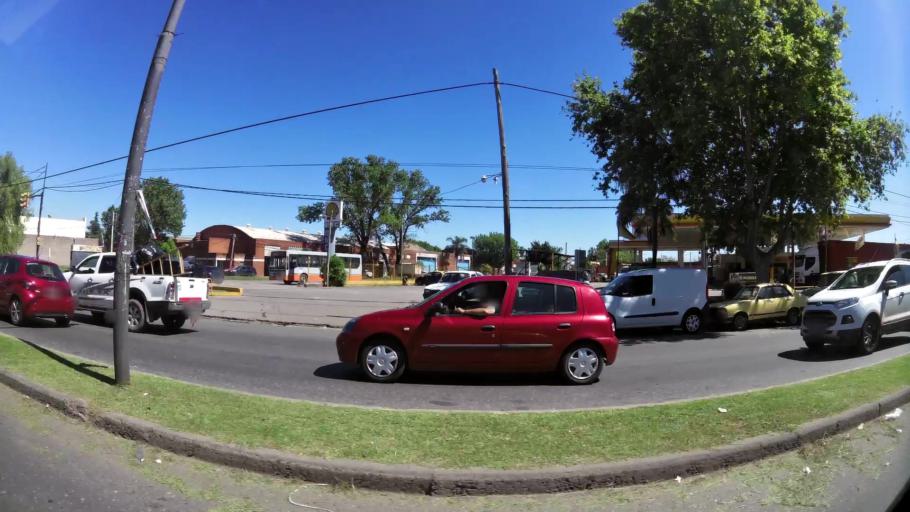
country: AR
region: Santa Fe
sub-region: Departamento de Rosario
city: Rosario
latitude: -32.9627
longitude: -60.7010
